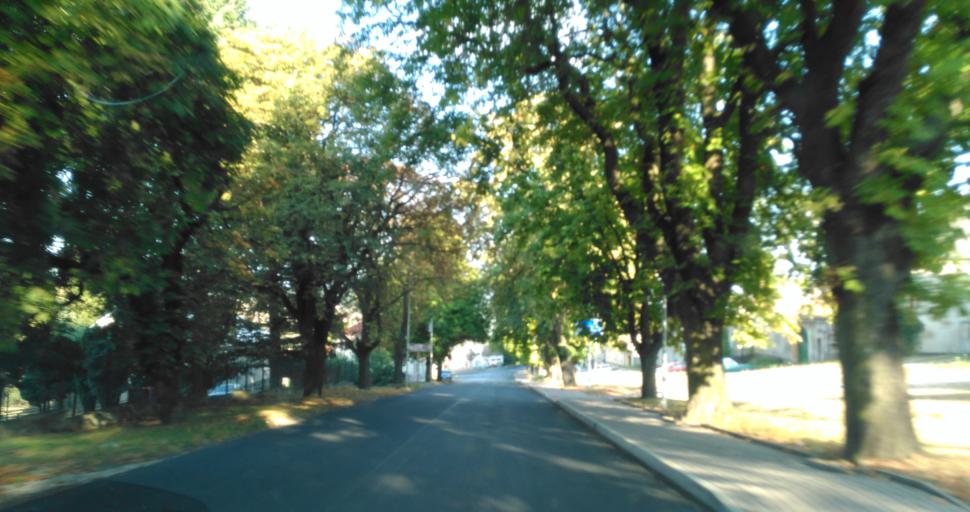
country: CZ
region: Central Bohemia
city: Hudlice
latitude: 49.9611
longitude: 13.9732
